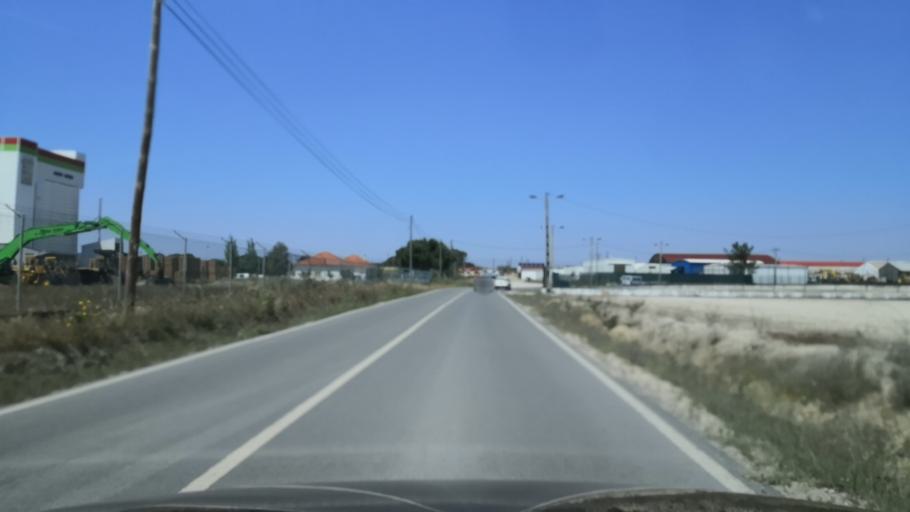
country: PT
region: Setubal
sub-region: Palmela
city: Palmela
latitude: 38.6317
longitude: -8.7468
